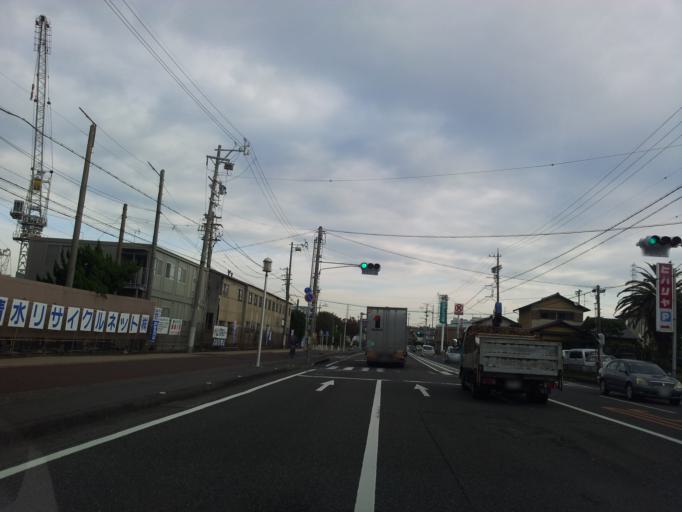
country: JP
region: Shizuoka
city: Shizuoka-shi
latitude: 34.9850
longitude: 138.5068
